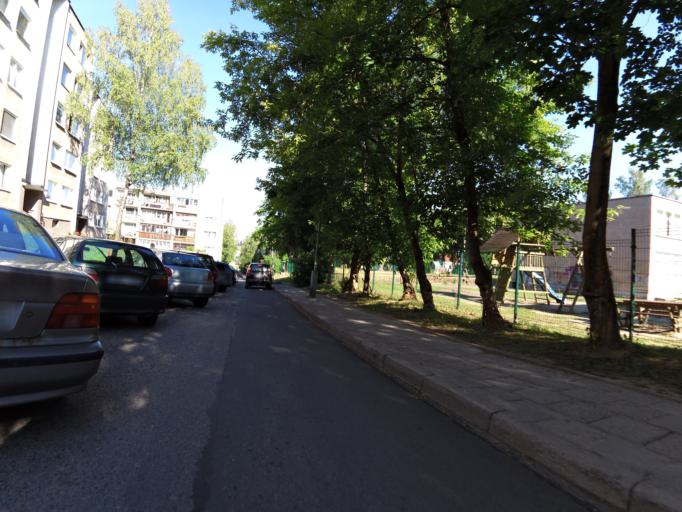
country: LT
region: Vilnius County
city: Rasos
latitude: 54.7027
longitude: 25.3189
